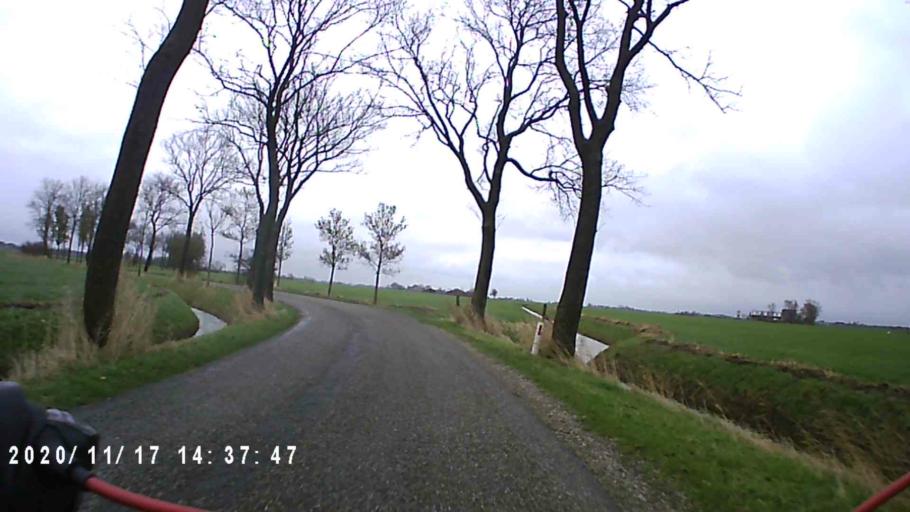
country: NL
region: Groningen
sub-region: Gemeente Zuidhorn
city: Oldehove
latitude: 53.2922
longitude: 6.3800
